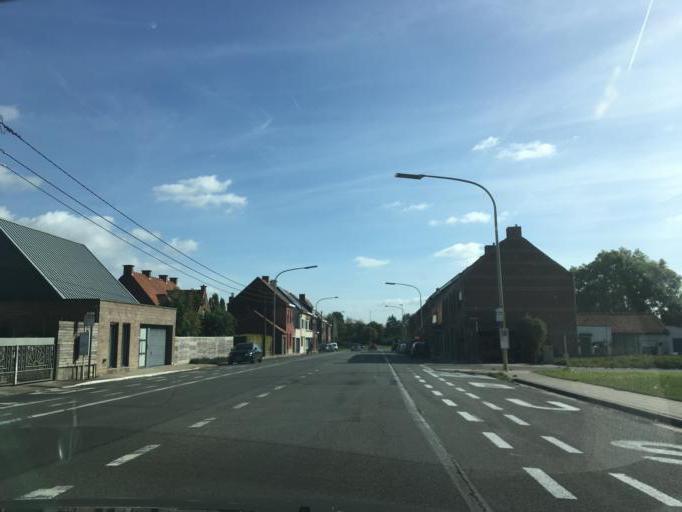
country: BE
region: Flanders
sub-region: Provincie West-Vlaanderen
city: Ieper
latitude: 50.8491
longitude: 2.9135
